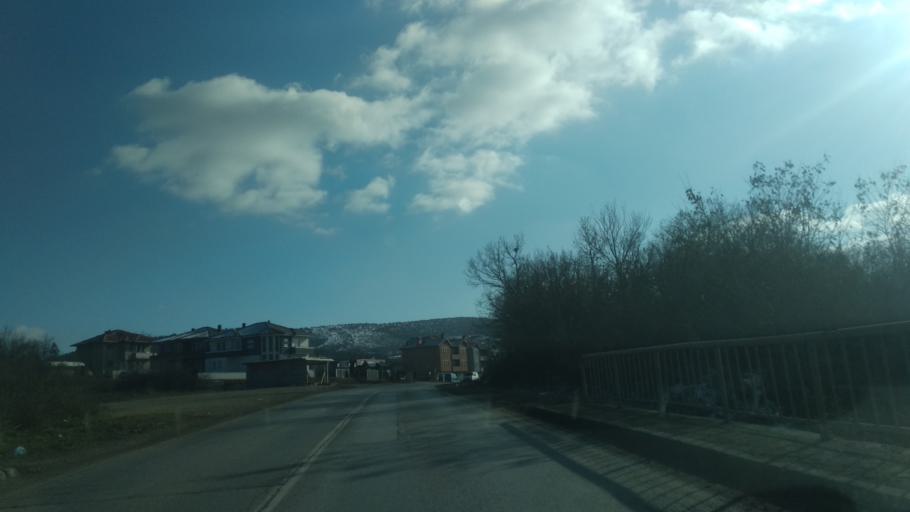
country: XK
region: Pristina
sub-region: Komuna e Prishtines
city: Pristina
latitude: 42.7434
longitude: 21.1406
